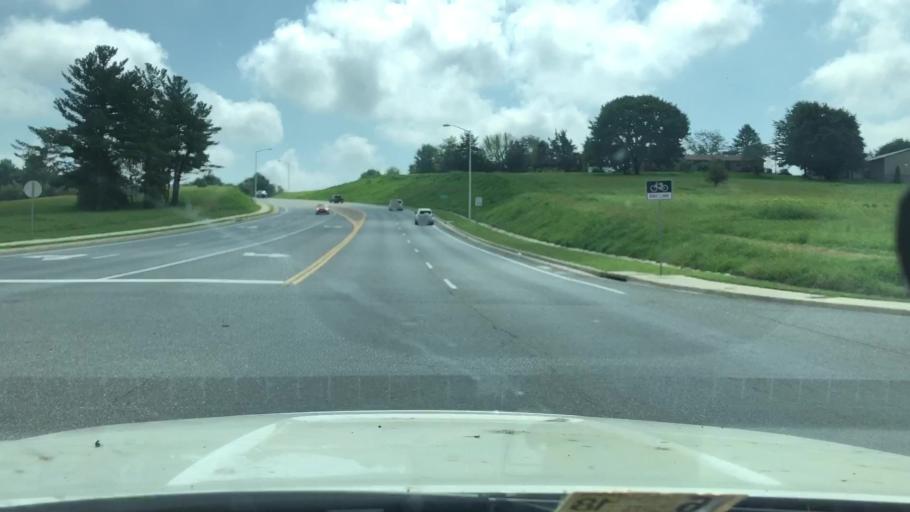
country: US
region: Virginia
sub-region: Rockingham County
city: Dayton
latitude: 38.4310
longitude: -78.9034
